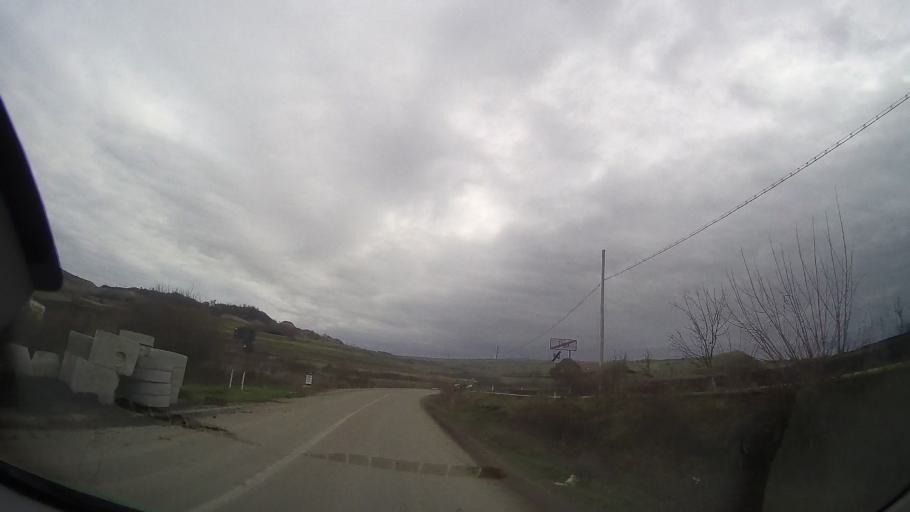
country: RO
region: Cluj
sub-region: Comuna Catina
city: Catina
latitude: 46.8180
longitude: 24.2241
